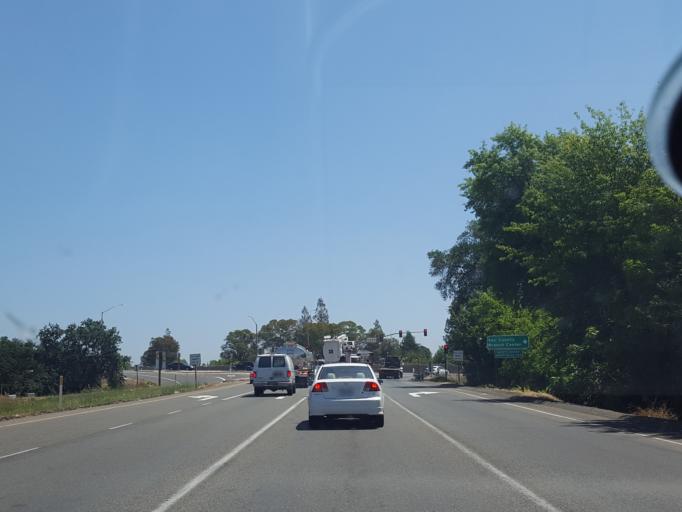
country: US
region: California
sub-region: Sacramento County
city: La Riviera
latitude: 38.5644
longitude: -121.3381
